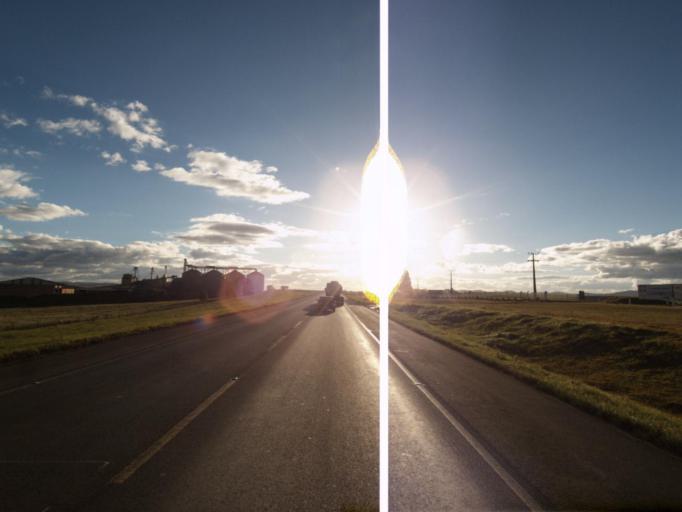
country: BR
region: Santa Catarina
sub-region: Campos Novos
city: Campos Novos
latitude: -27.3679
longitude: -51.2565
